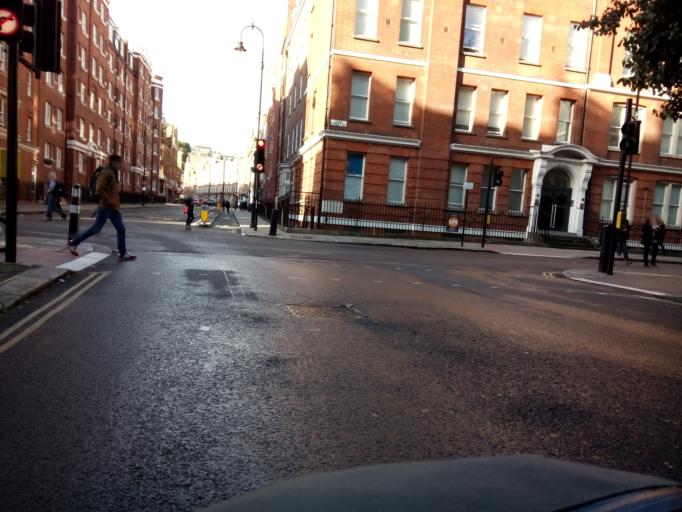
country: GB
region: England
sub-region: Greater London
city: Clerkenwell
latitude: 51.5264
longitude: -0.1234
